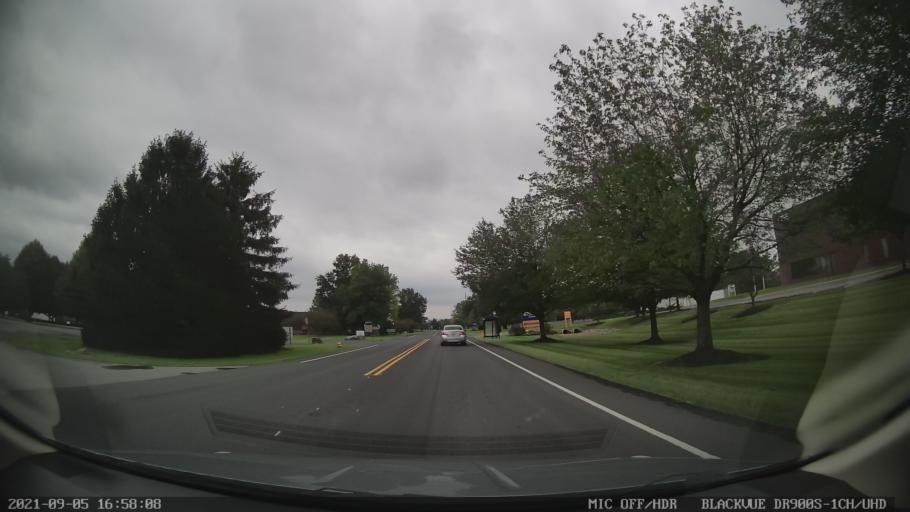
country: US
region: Pennsylvania
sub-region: Lehigh County
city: Trexlertown
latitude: 40.5930
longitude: -75.6088
